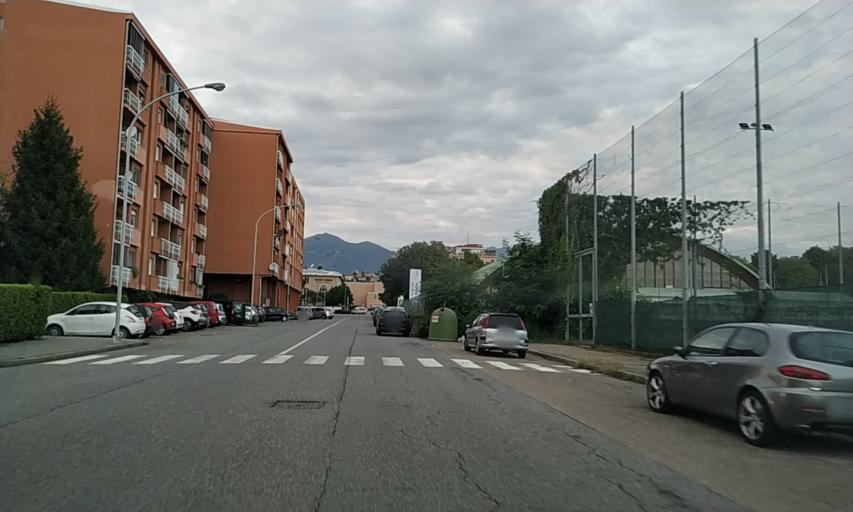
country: IT
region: Piedmont
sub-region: Provincia di Biella
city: Ponderano
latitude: 45.5513
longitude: 8.0547
